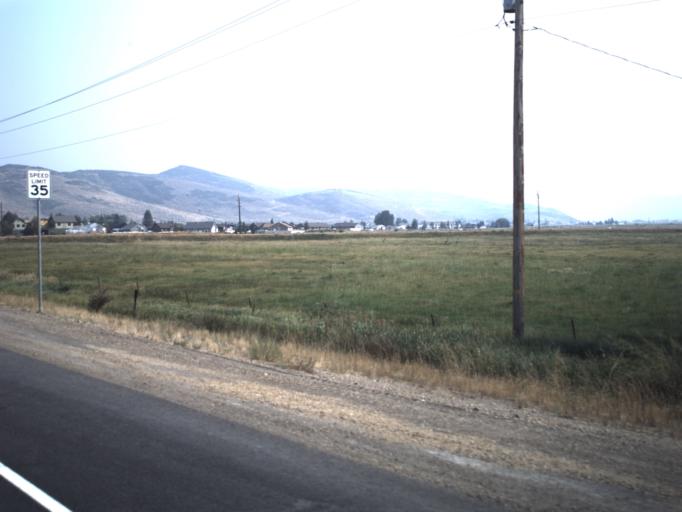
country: US
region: Utah
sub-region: Summit County
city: Kamas
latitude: 40.6399
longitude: -111.2890
